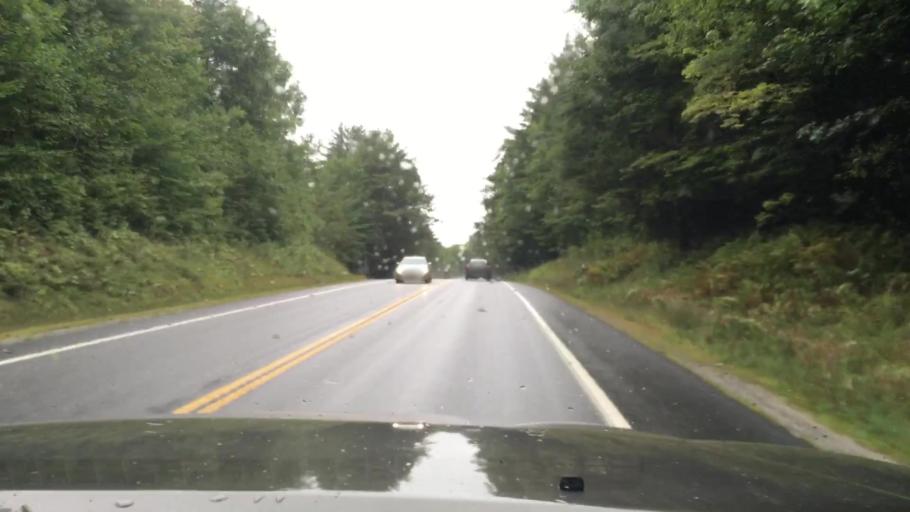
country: US
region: New Hampshire
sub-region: Hillsborough County
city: Antrim
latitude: 43.0697
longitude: -72.0527
